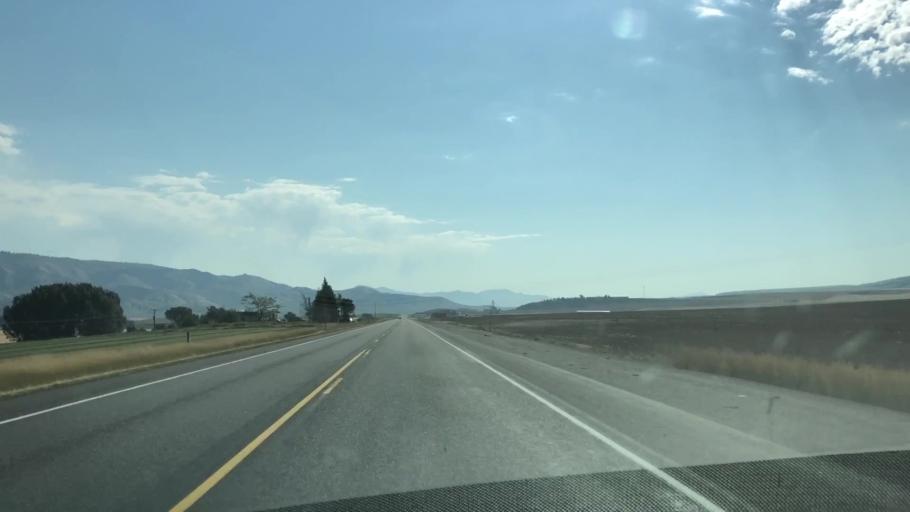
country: US
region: Idaho
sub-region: Jefferson County
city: Rigby
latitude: 43.6113
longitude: -111.7094
